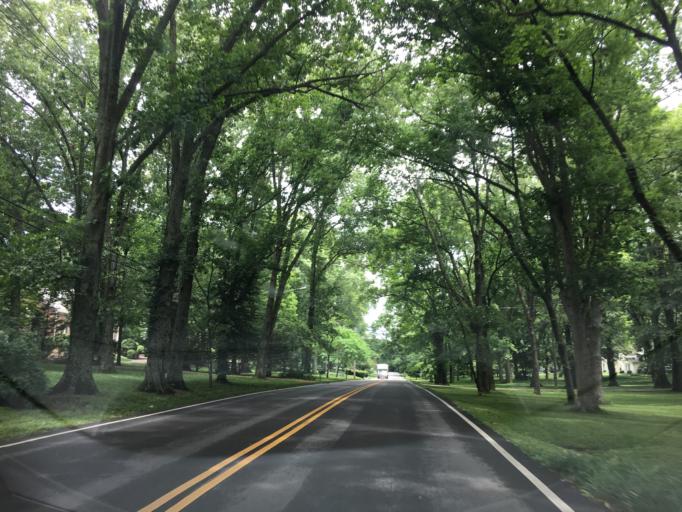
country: US
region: Tennessee
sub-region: Davidson County
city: Belle Meade
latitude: 36.0983
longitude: -86.8465
